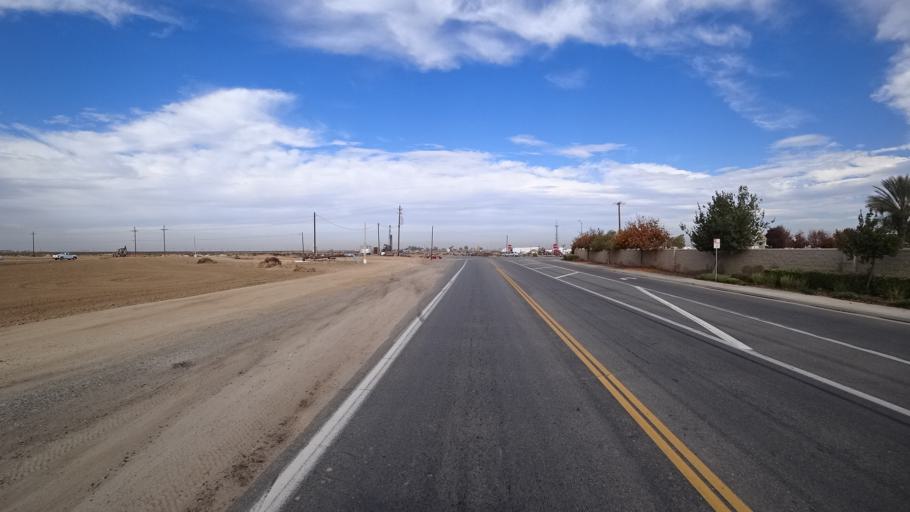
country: US
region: California
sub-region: Kern County
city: Rosedale
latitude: 35.4262
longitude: -119.1455
